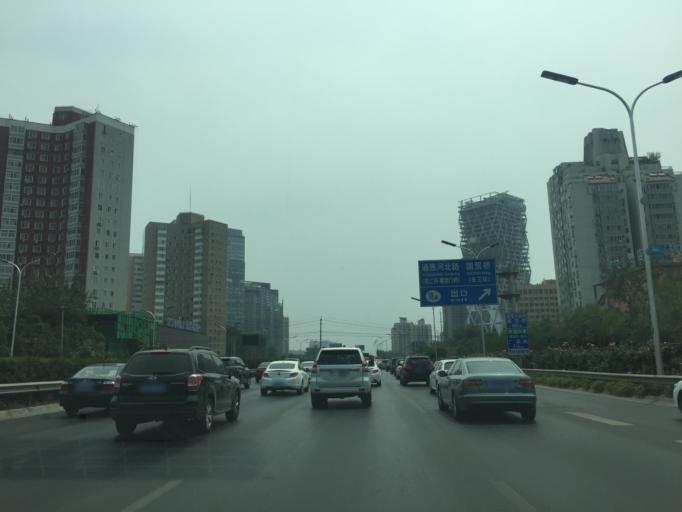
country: CN
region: Beijing
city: Dongfeng
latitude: 39.9185
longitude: 116.4836
